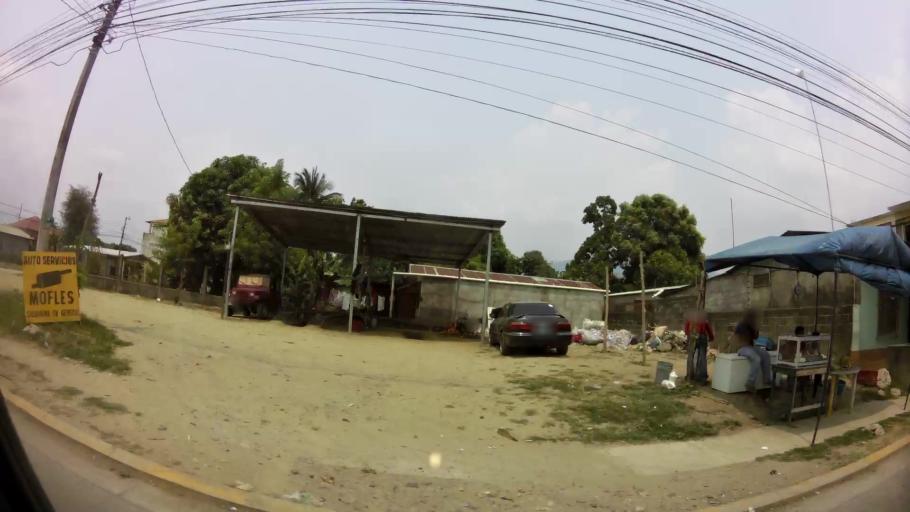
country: HN
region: Yoro
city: El Progreso
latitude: 15.4038
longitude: -87.8051
